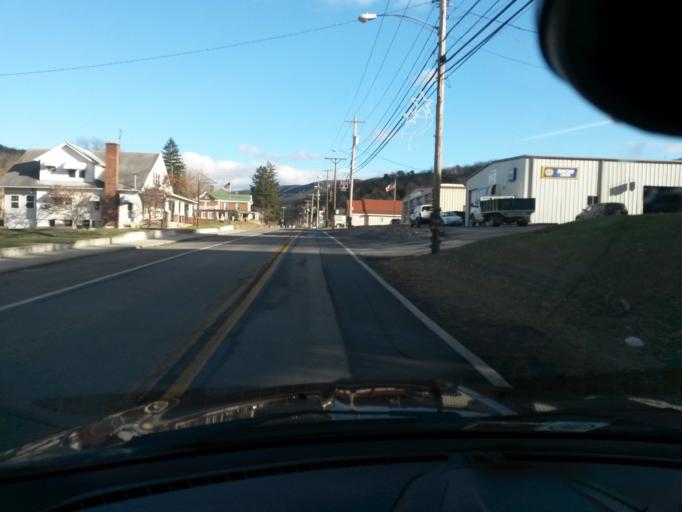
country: US
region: Virginia
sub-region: Giles County
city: Narrows
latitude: 37.3965
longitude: -80.7961
